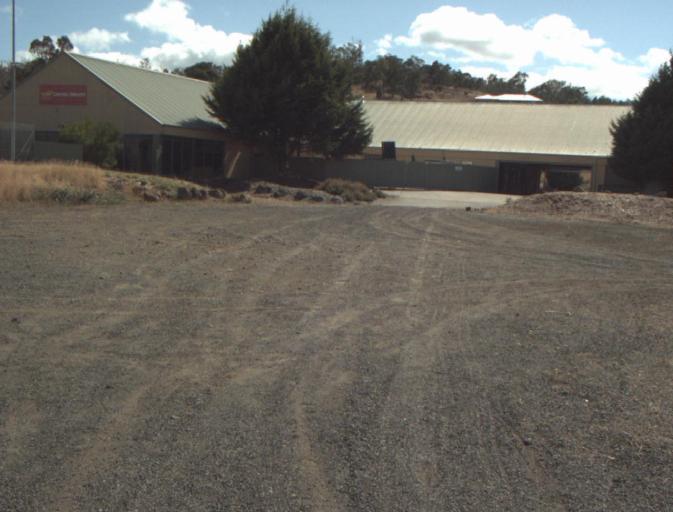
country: AU
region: Tasmania
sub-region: Launceston
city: Newstead
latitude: -41.4196
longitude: 147.1852
